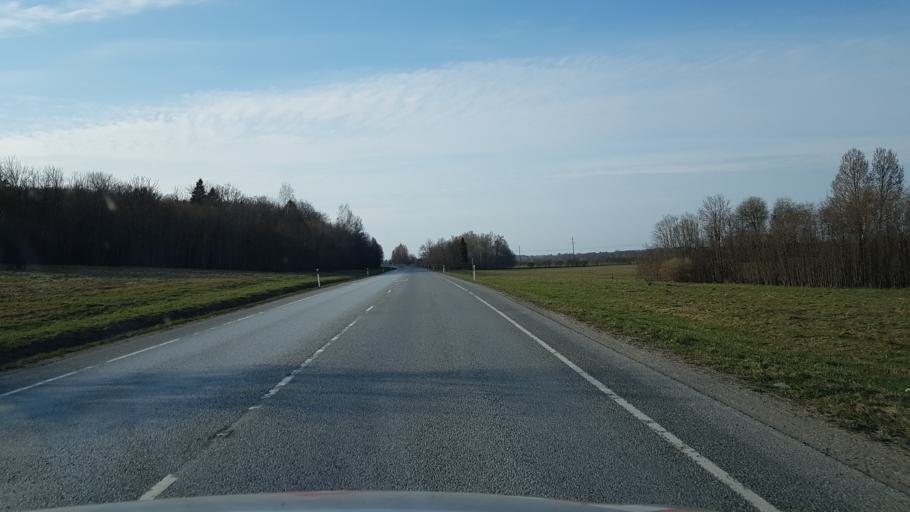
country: EE
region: Laeaene-Virumaa
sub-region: Haljala vald
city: Haljala
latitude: 59.3973
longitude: 26.3079
